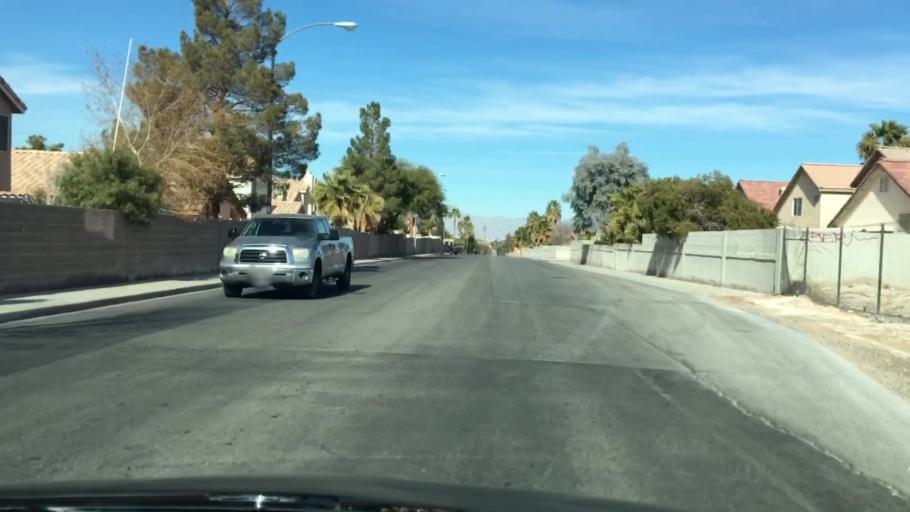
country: US
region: Nevada
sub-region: Clark County
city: Paradise
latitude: 36.0369
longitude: -115.1407
